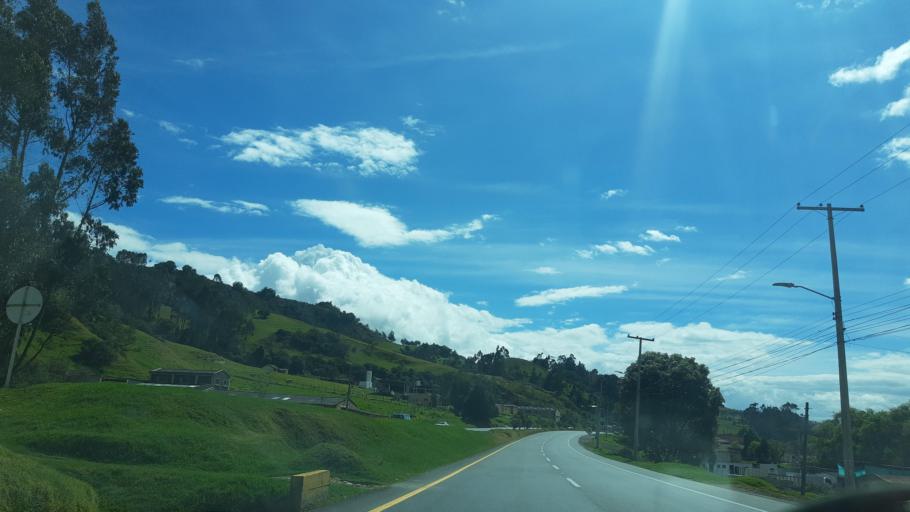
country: CO
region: Cundinamarca
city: Villapinzon
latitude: 5.2029
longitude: -73.6046
